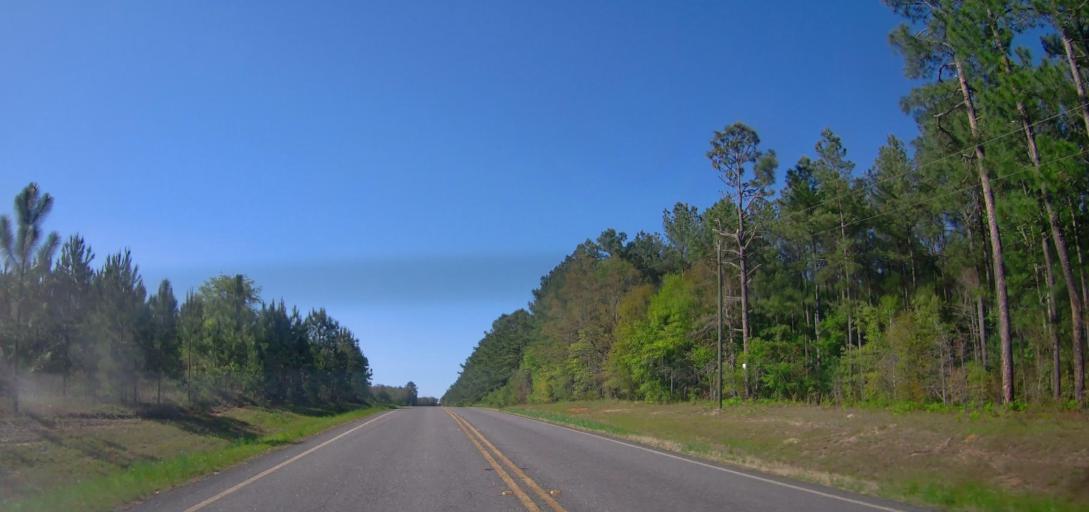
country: US
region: Georgia
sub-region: Wilcox County
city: Rochelle
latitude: 32.0235
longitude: -83.4996
